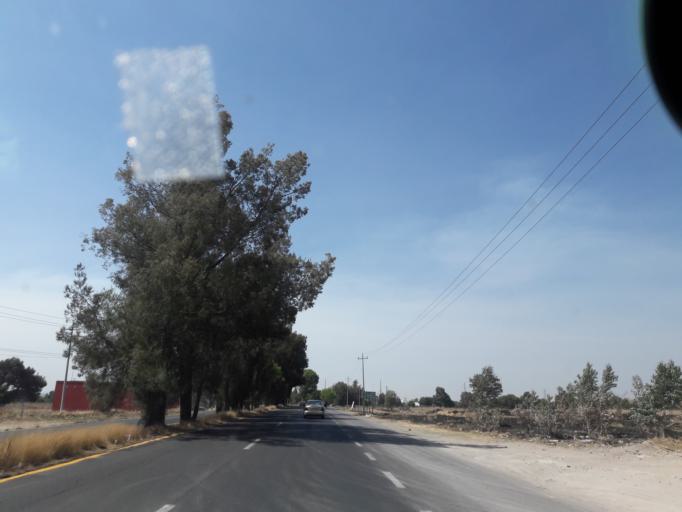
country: MX
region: Tlaxcala
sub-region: Santa Cruz Quilehtla
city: Ayometitla
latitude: 19.1944
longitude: -98.1950
